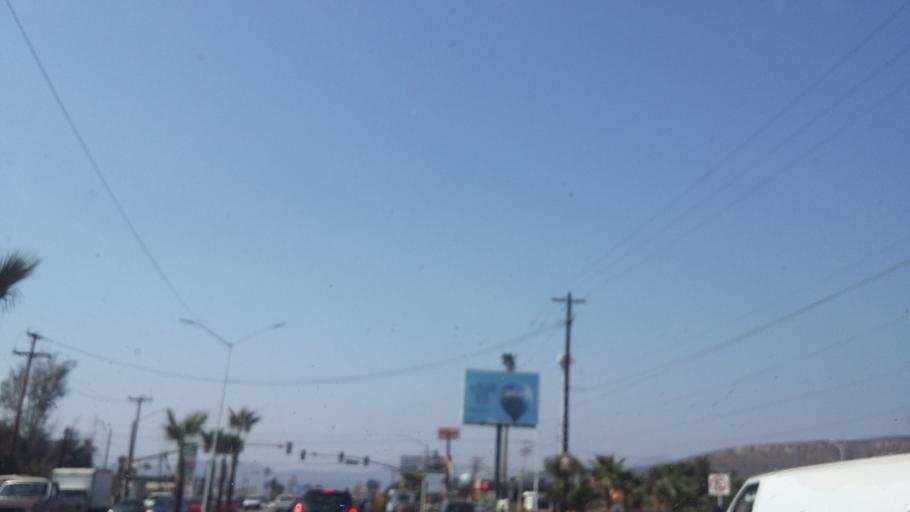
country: MX
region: Baja California
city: Ensenada
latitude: 31.8088
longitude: -116.5963
